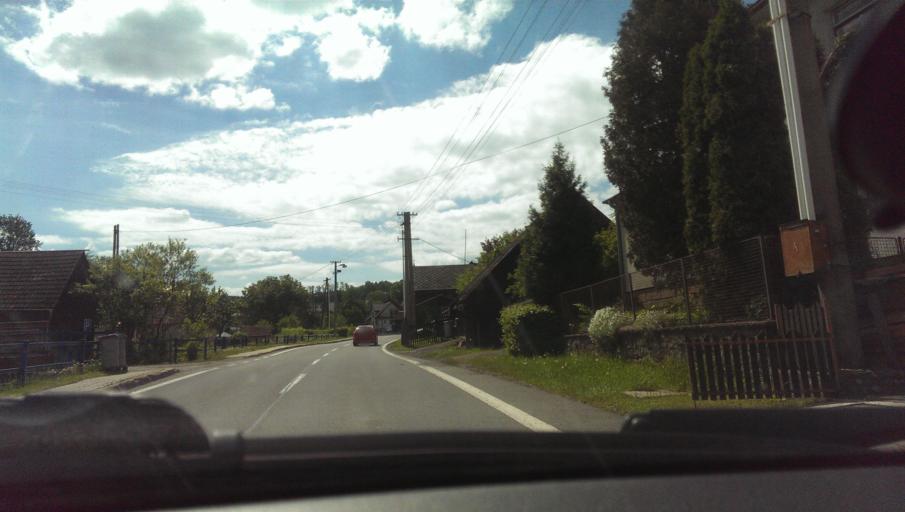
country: CZ
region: Zlin
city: Valasska Polanka
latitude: 49.2357
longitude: 17.9544
